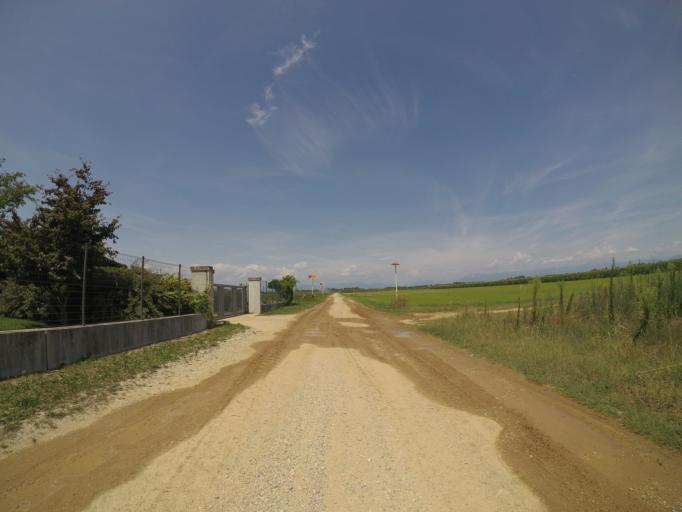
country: IT
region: Friuli Venezia Giulia
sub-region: Provincia di Udine
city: Talmassons
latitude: 45.9629
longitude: 13.0998
